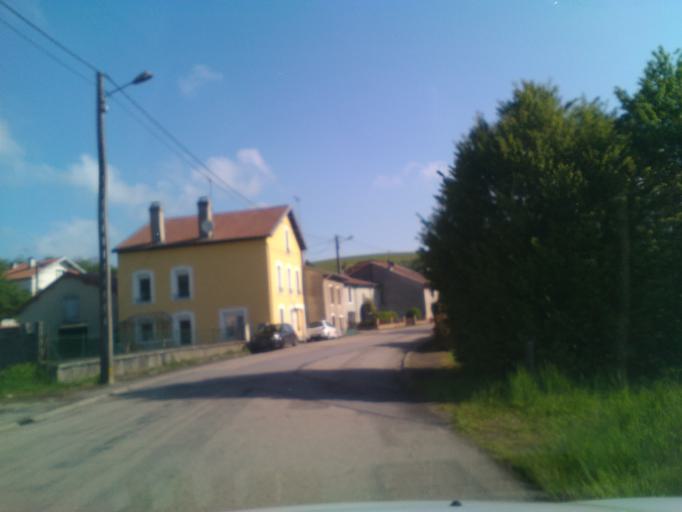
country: FR
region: Lorraine
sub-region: Departement des Vosges
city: Mirecourt
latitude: 48.3459
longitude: 6.1391
